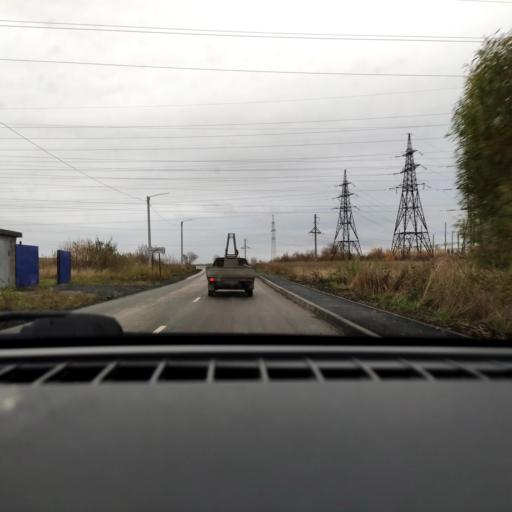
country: RU
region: Perm
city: Ferma
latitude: 57.9202
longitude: 56.3058
